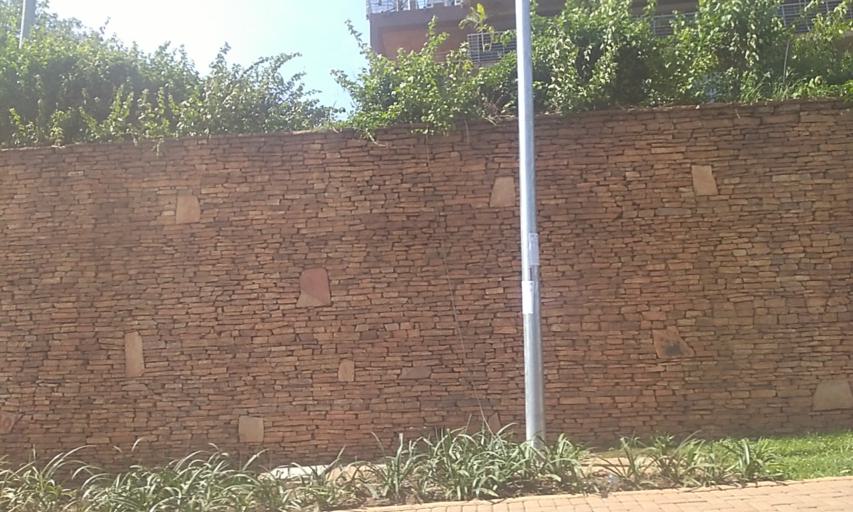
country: UG
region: Central Region
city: Kampala Central Division
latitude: 0.3492
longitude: 32.6001
